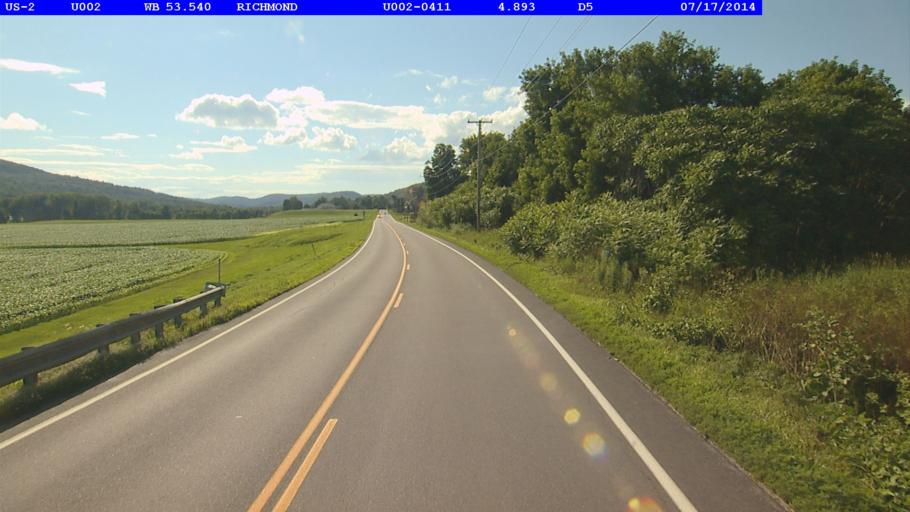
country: US
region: Vermont
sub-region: Chittenden County
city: Jericho
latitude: 44.3951
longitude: -72.9553
